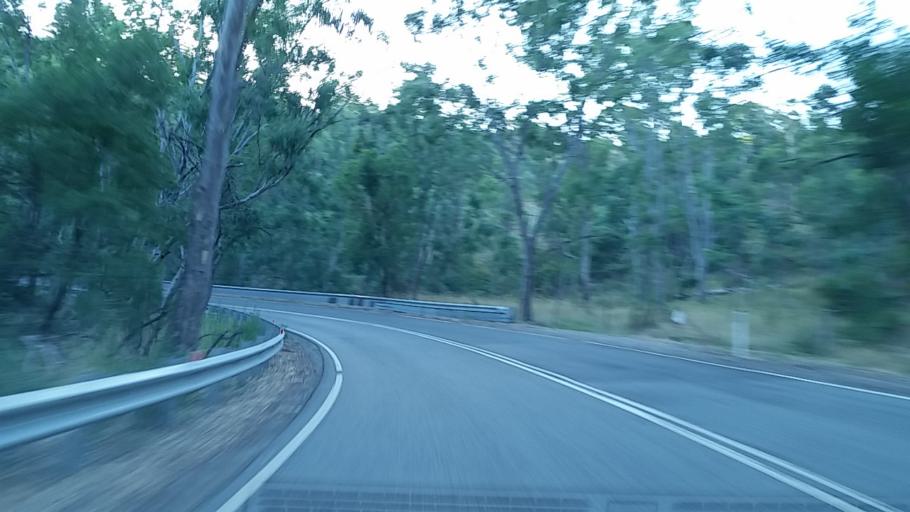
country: AU
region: South Australia
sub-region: Campbelltown
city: Athelstone
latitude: -34.8573
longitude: 138.7878
